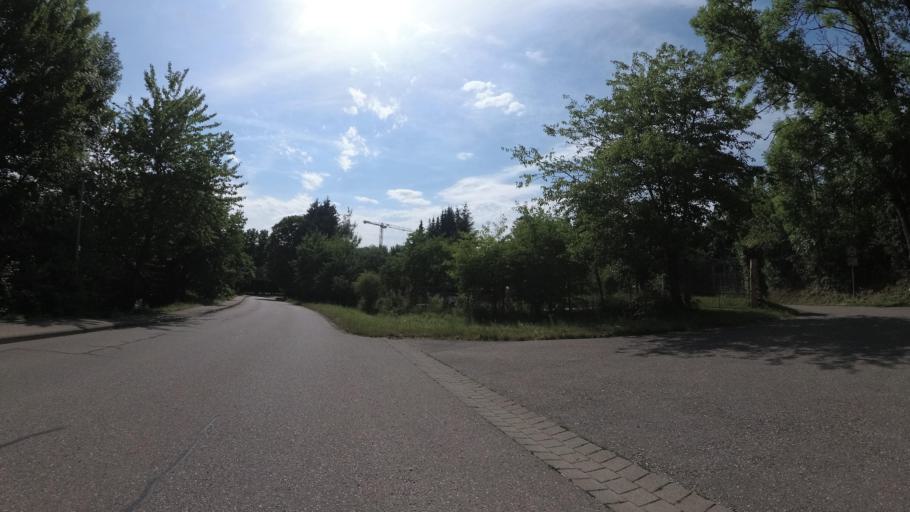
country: DE
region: Baden-Wuerttemberg
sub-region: Regierungsbezirk Stuttgart
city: Neckarsulm
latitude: 49.1904
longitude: 9.2378
